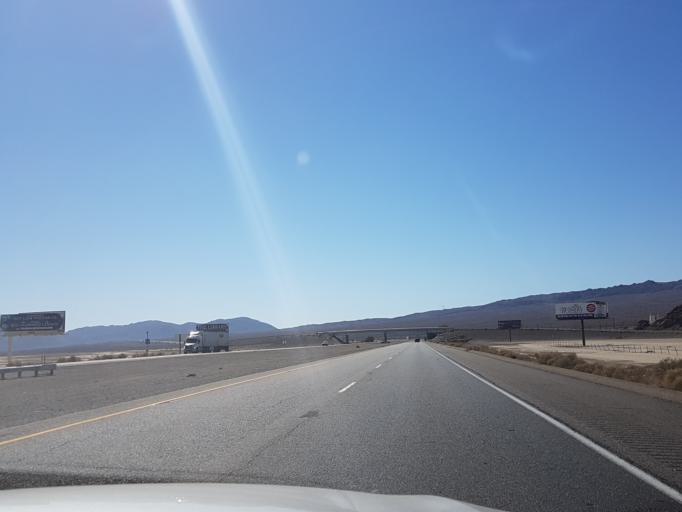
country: US
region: California
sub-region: San Bernardino County
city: Fort Irwin
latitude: 35.2593
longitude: -116.0801
